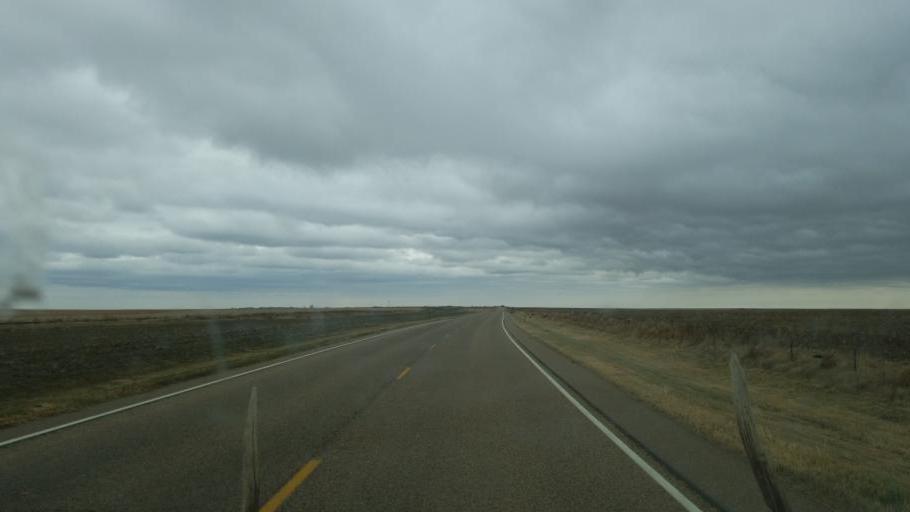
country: US
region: Colorado
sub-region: Cheyenne County
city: Cheyenne Wells
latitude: 38.8171
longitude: -102.4905
